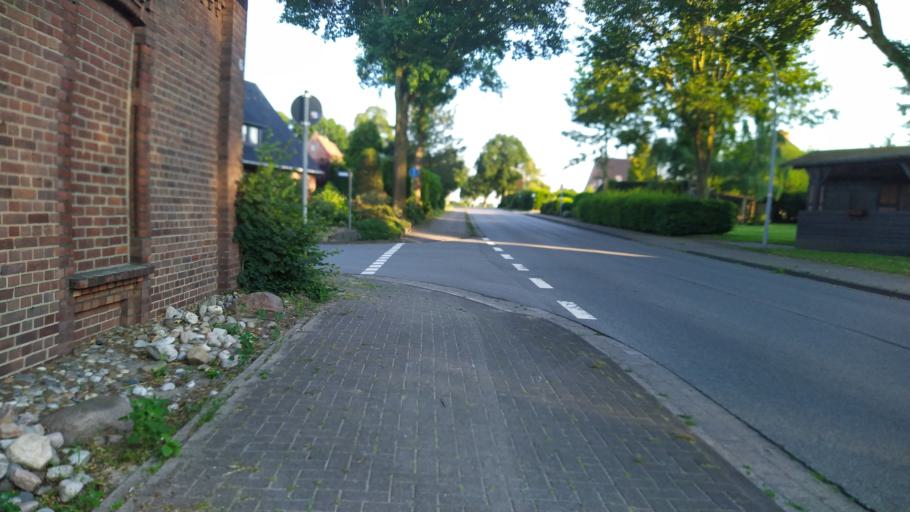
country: DE
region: Lower Saxony
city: Ebersdorf
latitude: 53.5237
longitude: 9.0583
